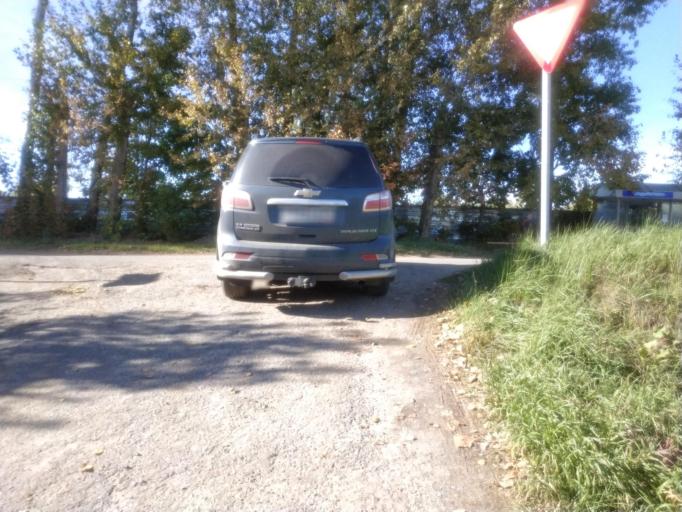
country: RU
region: Chuvashia
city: Novyye Lapsary
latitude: 56.1426
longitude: 47.1449
